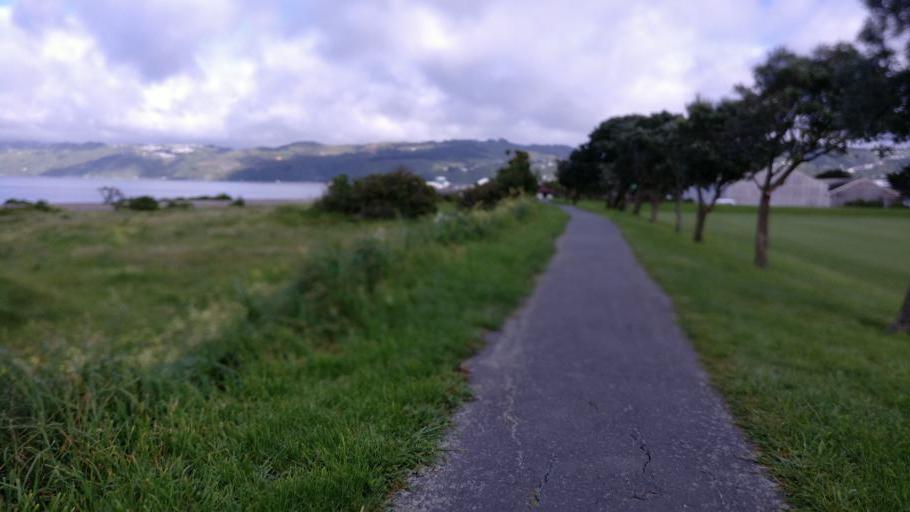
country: NZ
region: Wellington
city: Petone
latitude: -41.2349
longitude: 174.8946
